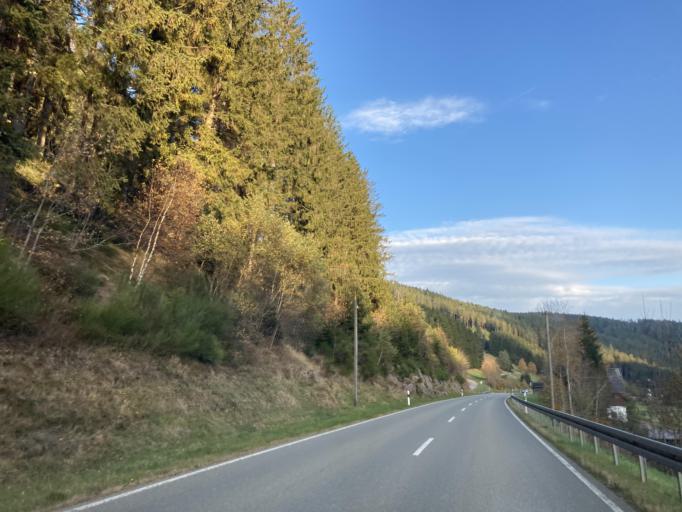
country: DE
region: Baden-Wuerttemberg
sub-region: Freiburg Region
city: Vohrenbach
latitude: 48.0080
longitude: 8.2826
